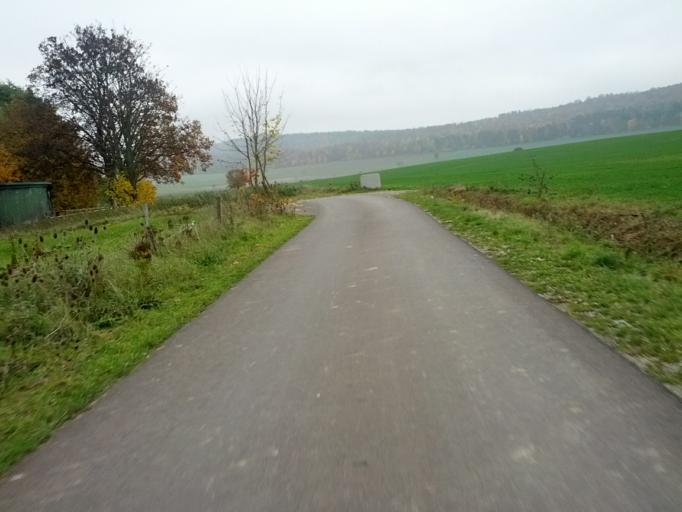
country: DE
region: Thuringia
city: Seebach
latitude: 50.9796
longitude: 10.4190
